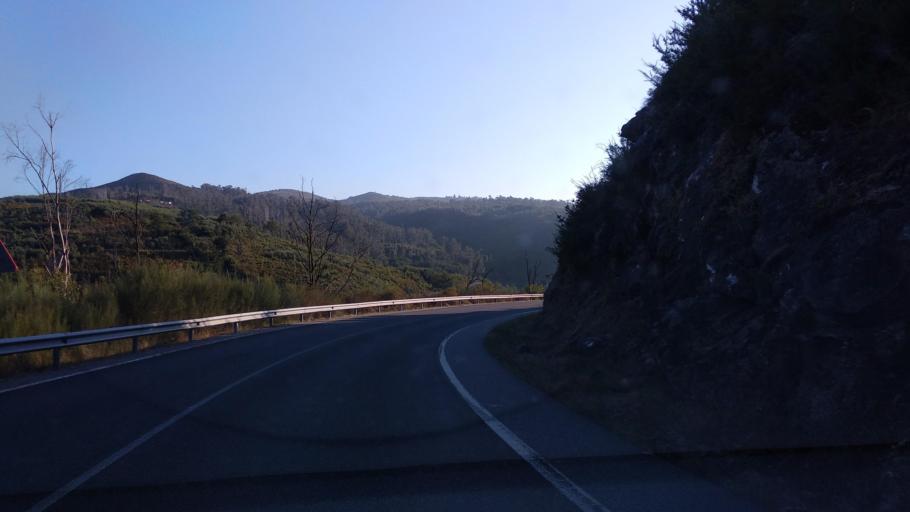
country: ES
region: Galicia
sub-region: Provincia de Pontevedra
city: Ponte Caldelas
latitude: 42.3419
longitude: -8.5442
